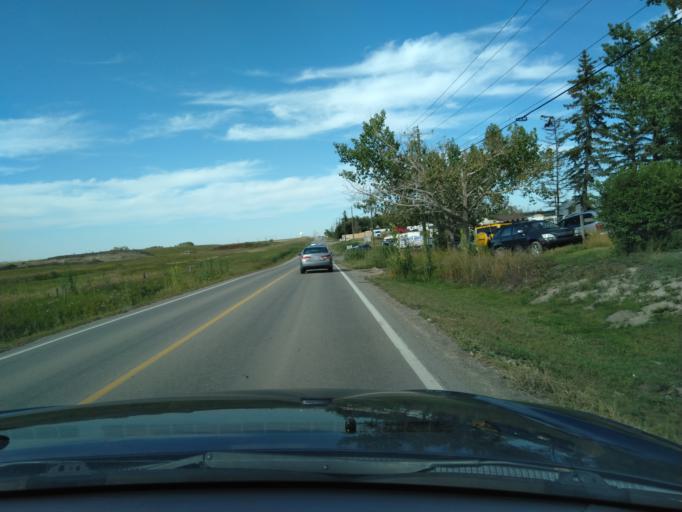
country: CA
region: Alberta
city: Calgary
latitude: 51.1186
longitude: -113.9817
